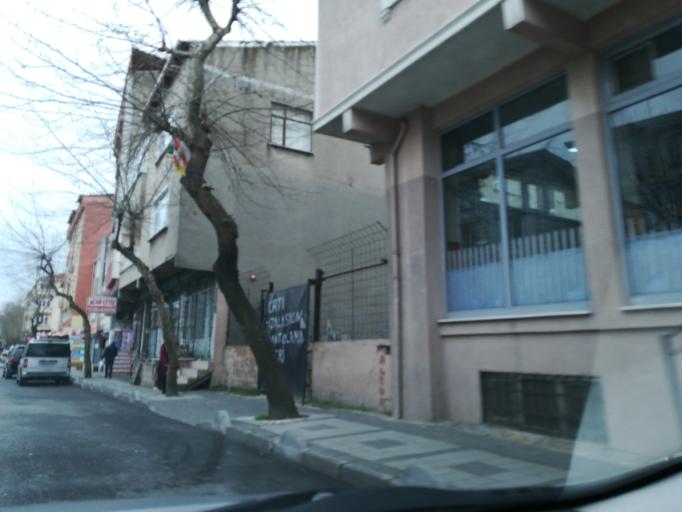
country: TR
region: Istanbul
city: Bagcilar
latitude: 41.0276
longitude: 28.8440
